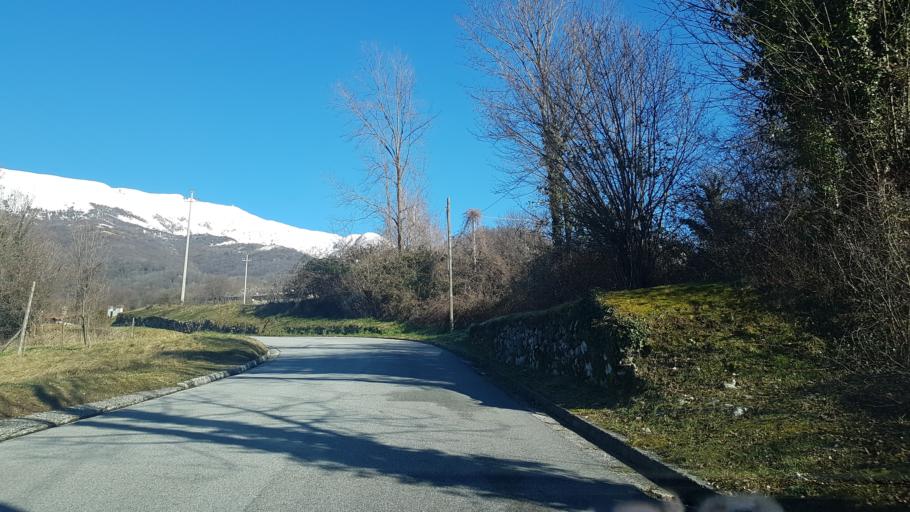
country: IT
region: Friuli Venezia Giulia
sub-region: Provincia di Udine
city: Montenars
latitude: 46.2513
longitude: 13.1647
